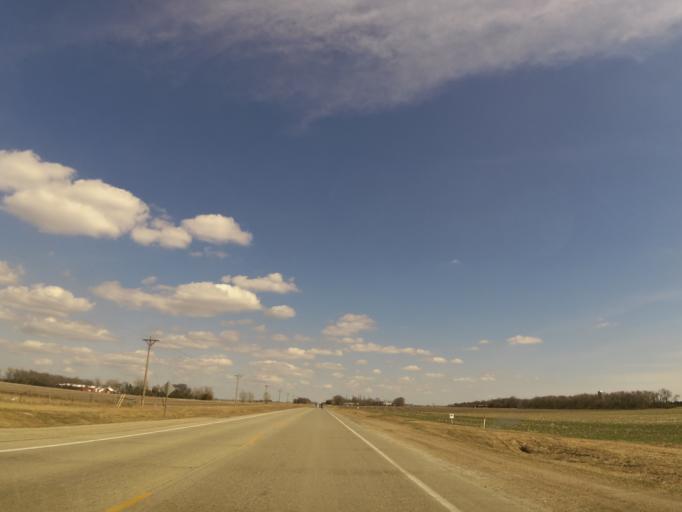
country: US
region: South Dakota
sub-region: Codington County
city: Watertown
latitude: 44.8900
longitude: -97.0364
